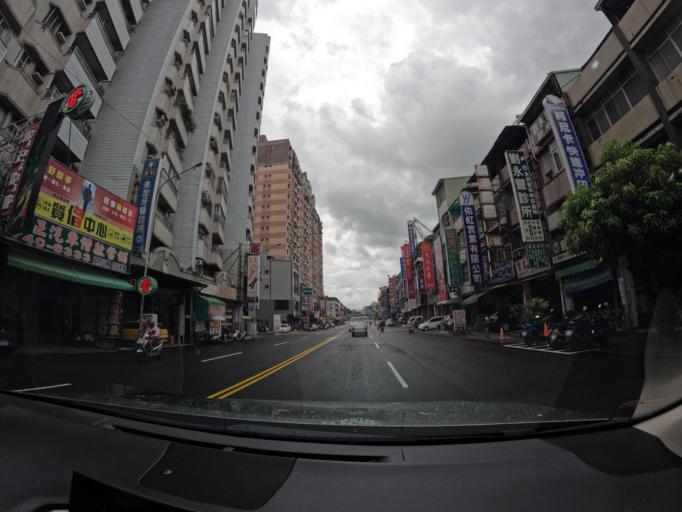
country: TW
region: Taiwan
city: Fengshan
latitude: 22.6290
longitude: 120.3404
